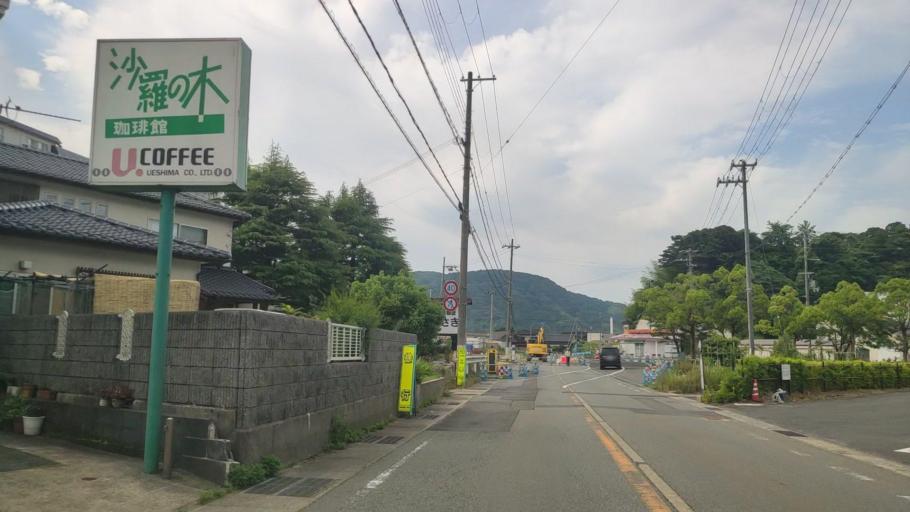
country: JP
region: Hyogo
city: Toyooka
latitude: 35.6305
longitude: 134.8163
